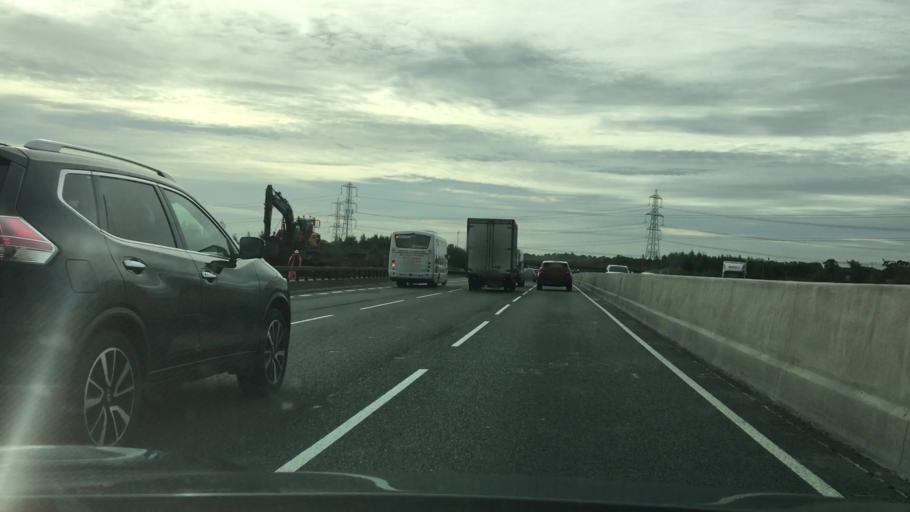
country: GB
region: England
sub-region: Leicestershire
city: Kegworth
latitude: 52.8596
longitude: -1.3018
